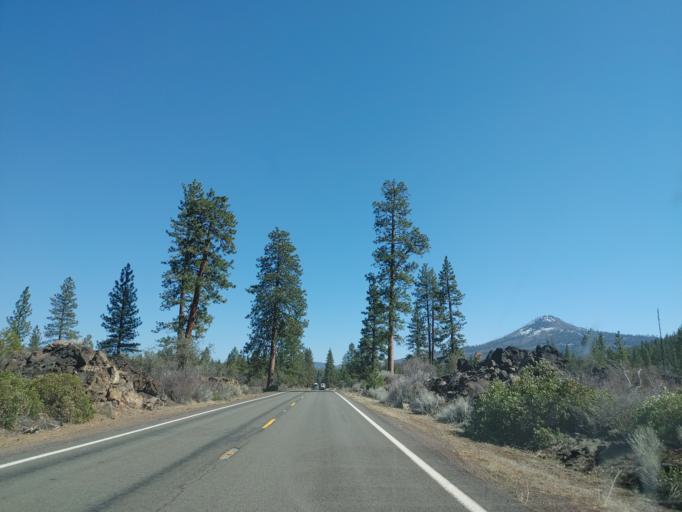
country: US
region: California
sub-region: Shasta County
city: Burney
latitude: 40.7513
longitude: -121.4881
